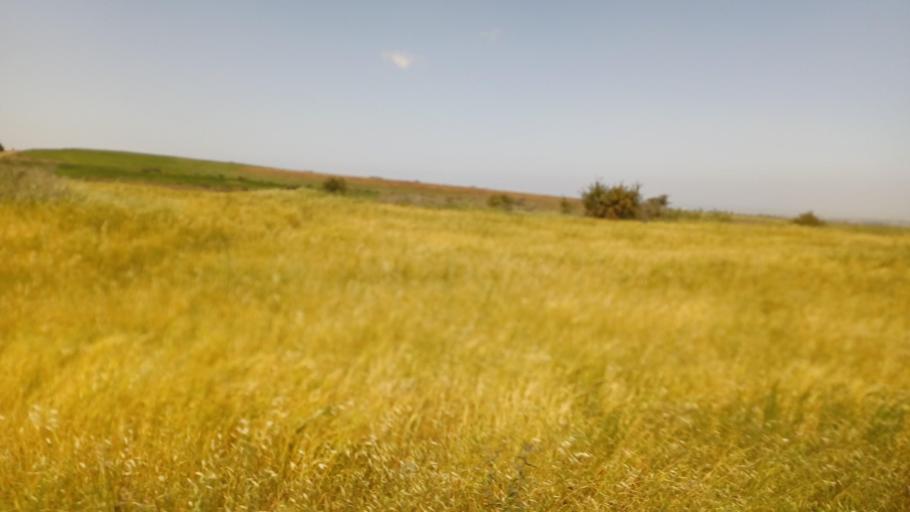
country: CY
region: Lefkosia
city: Lefka
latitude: 35.0970
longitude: 32.9349
